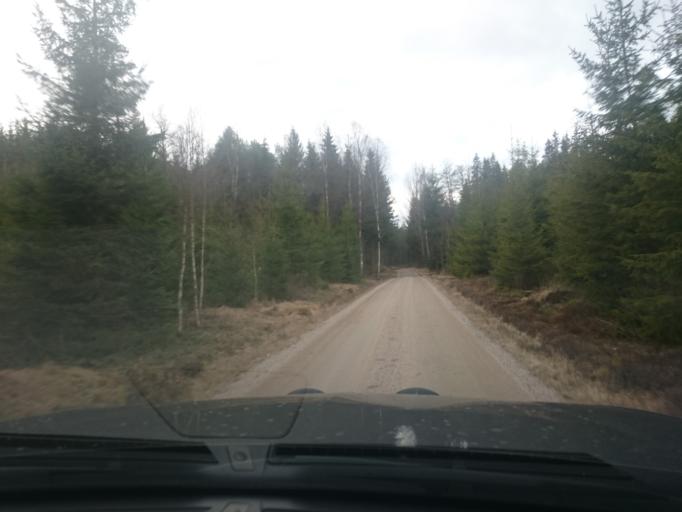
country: SE
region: Joenkoeping
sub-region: Vetlanda Kommun
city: Vetlanda
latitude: 57.2888
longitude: 15.1626
